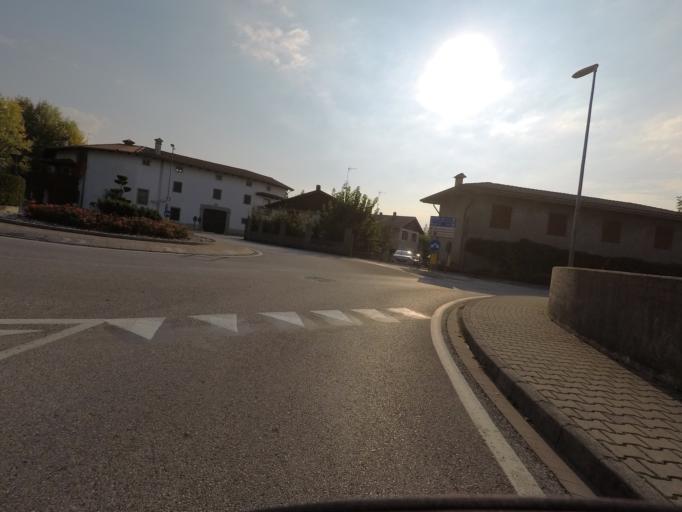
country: IT
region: Friuli Venezia Giulia
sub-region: Provincia di Udine
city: Artegna
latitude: 46.2356
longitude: 13.1545
